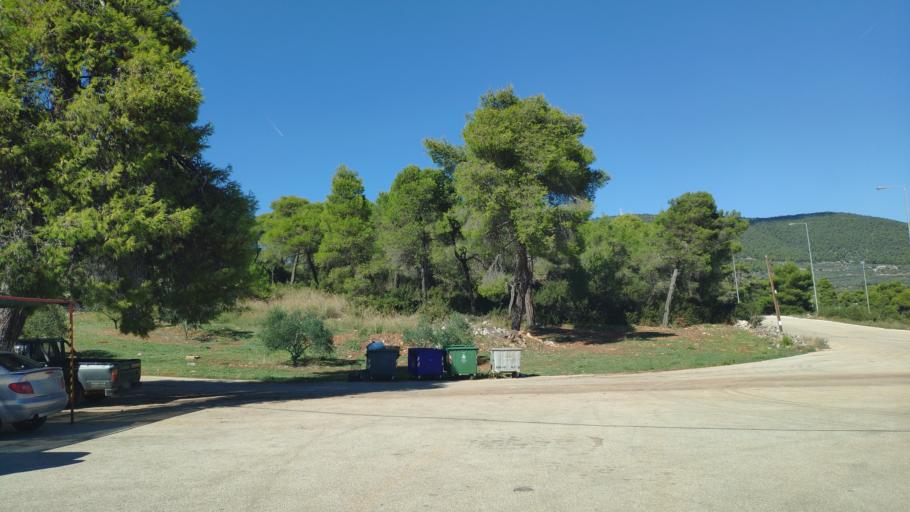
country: GR
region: Peloponnese
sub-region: Nomos Korinthias
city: Sofikon
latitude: 37.7859
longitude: 23.0760
